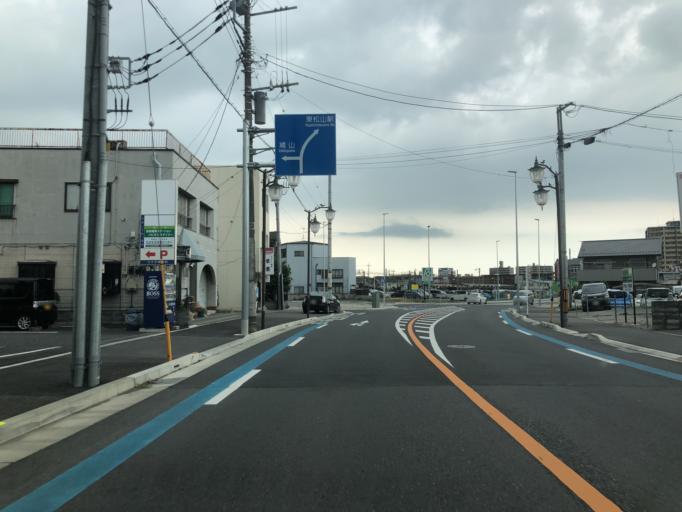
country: JP
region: Saitama
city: Sakado
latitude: 36.0322
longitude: 139.4034
